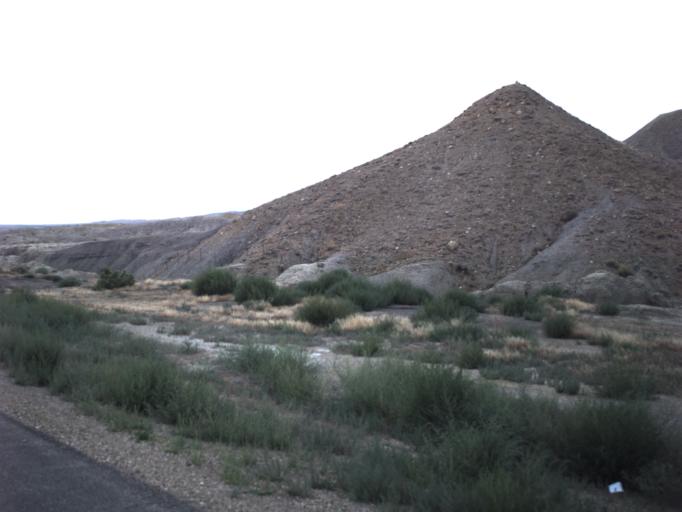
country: US
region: Utah
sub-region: Carbon County
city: East Carbon City
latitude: 39.2919
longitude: -110.3531
